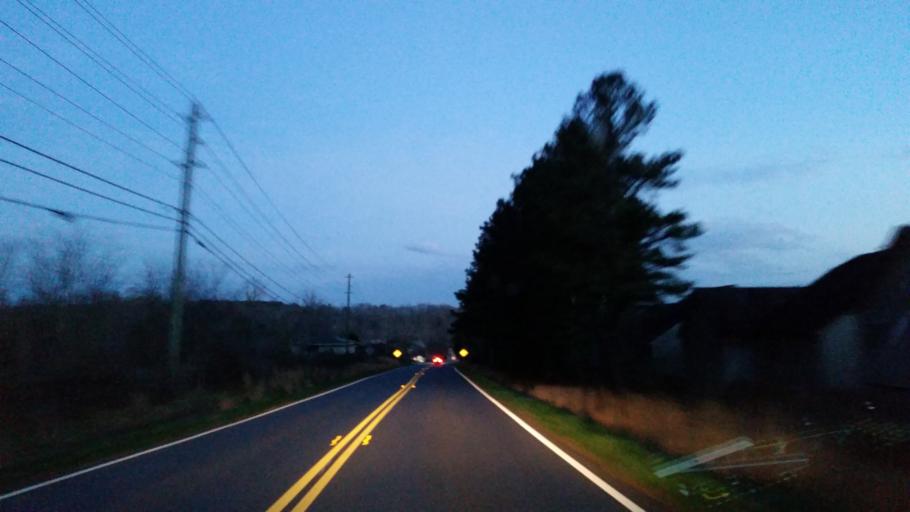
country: US
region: Georgia
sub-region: Cherokee County
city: Ball Ground
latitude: 34.2896
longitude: -84.4326
